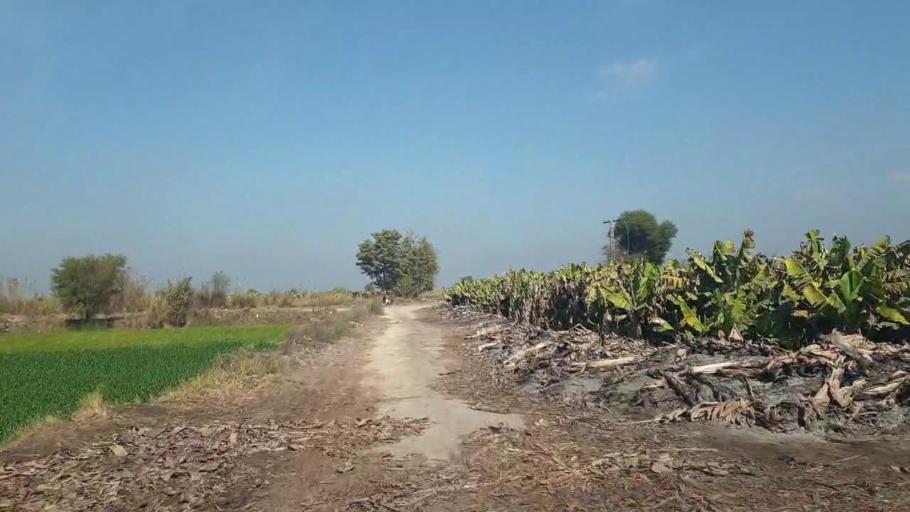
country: PK
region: Sindh
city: Shahdadpur
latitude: 25.9190
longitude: 68.5863
